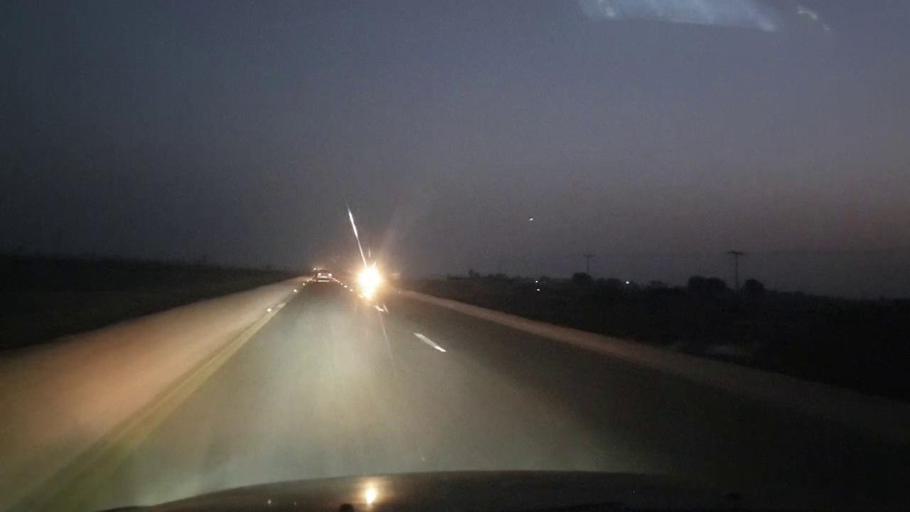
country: PK
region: Sindh
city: Chambar
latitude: 25.3394
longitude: 68.7948
